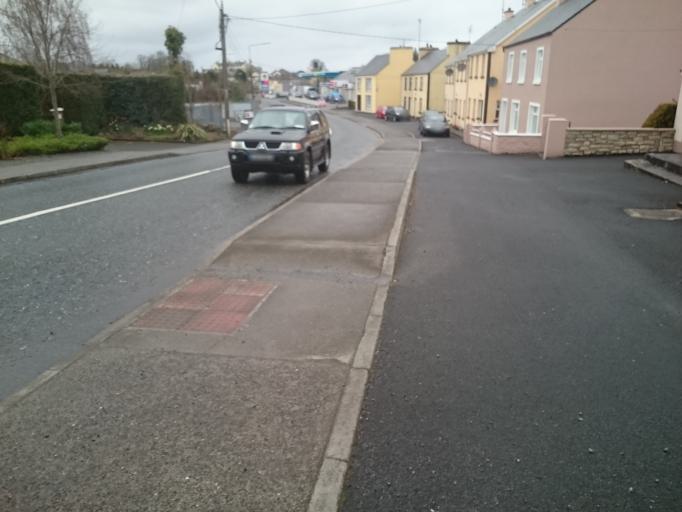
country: IE
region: Connaught
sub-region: Maigh Eo
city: Ballyhaunis
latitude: 53.7612
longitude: -8.7557
